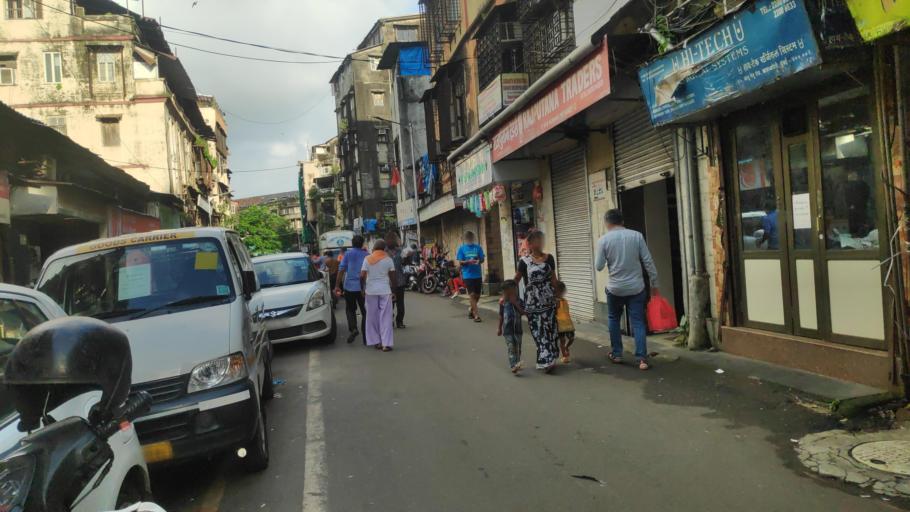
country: IN
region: Maharashtra
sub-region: Raigarh
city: Uran
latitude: 18.9477
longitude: 72.8293
